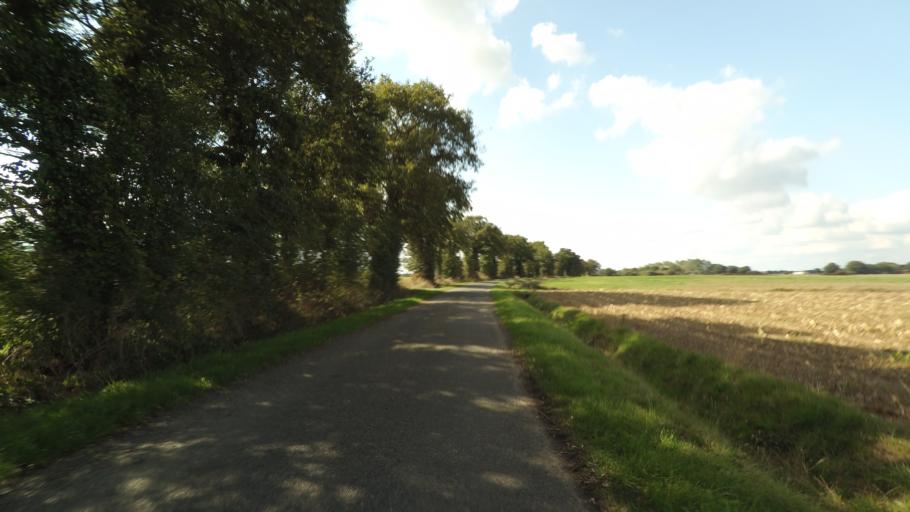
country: FR
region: Pays de la Loire
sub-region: Departement de la Vendee
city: Bouffere
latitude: 46.9672
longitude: -1.3827
